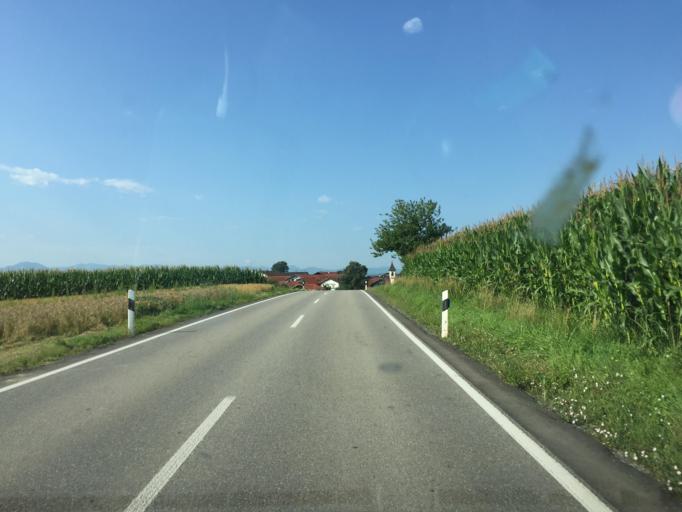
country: DE
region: Bavaria
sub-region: Upper Bavaria
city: Tuntenhausen
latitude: 47.9383
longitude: 12.0197
